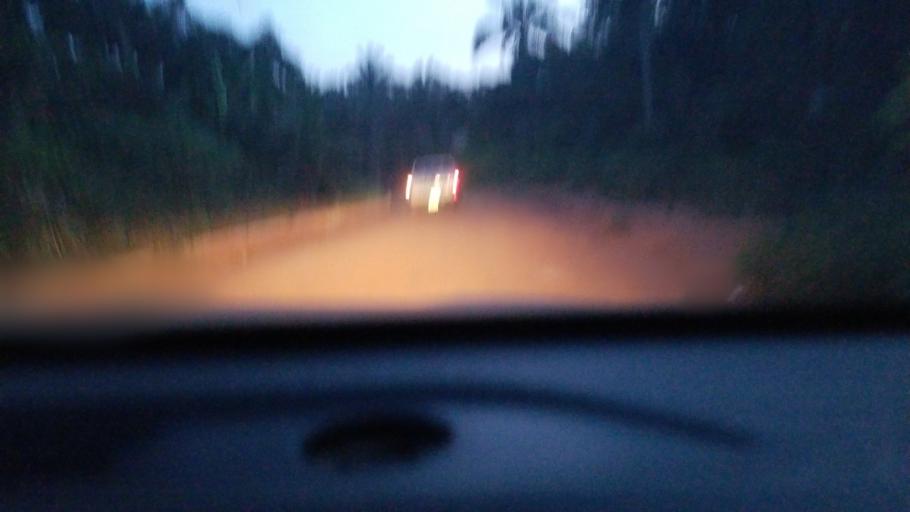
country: NG
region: Enugu
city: Obollo-Afor
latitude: 6.9046
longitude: 7.5095
